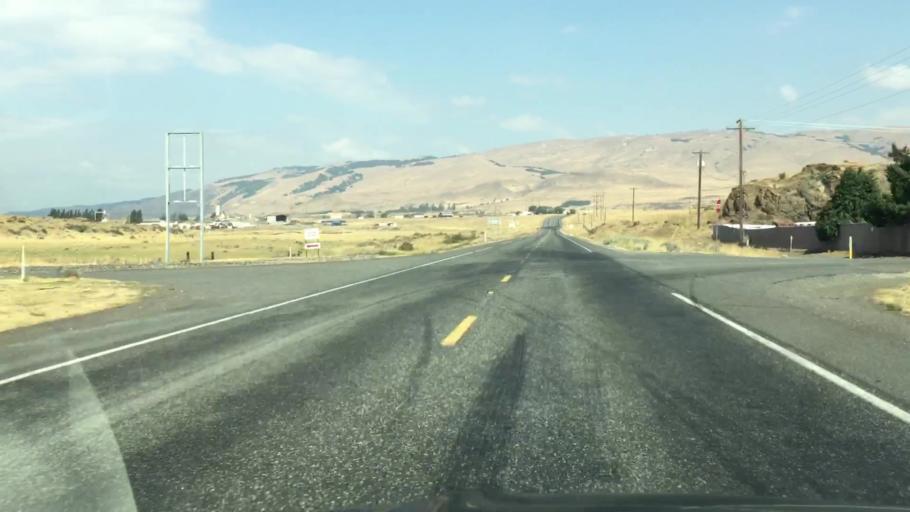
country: US
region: Washington
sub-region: Klickitat County
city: Dallesport
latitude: 45.6272
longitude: -121.1493
